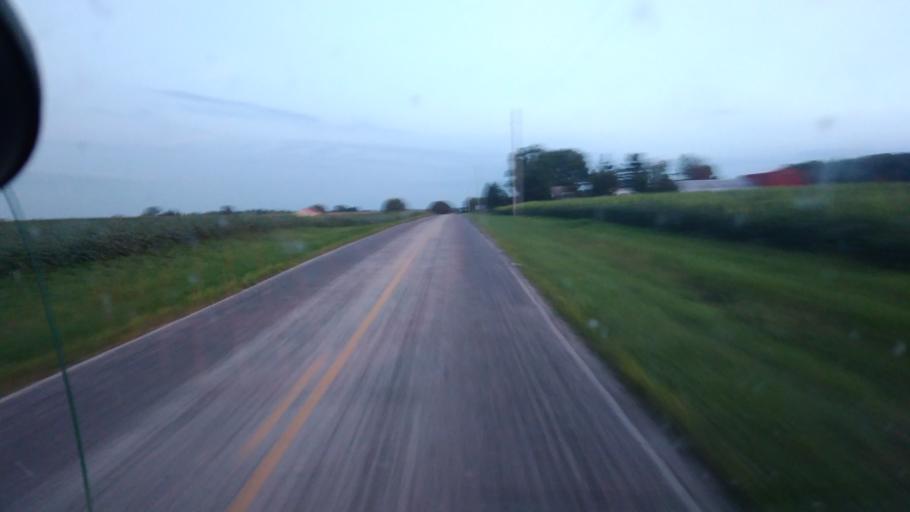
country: US
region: Ohio
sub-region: Hardin County
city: Kenton
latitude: 40.6320
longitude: -83.4574
